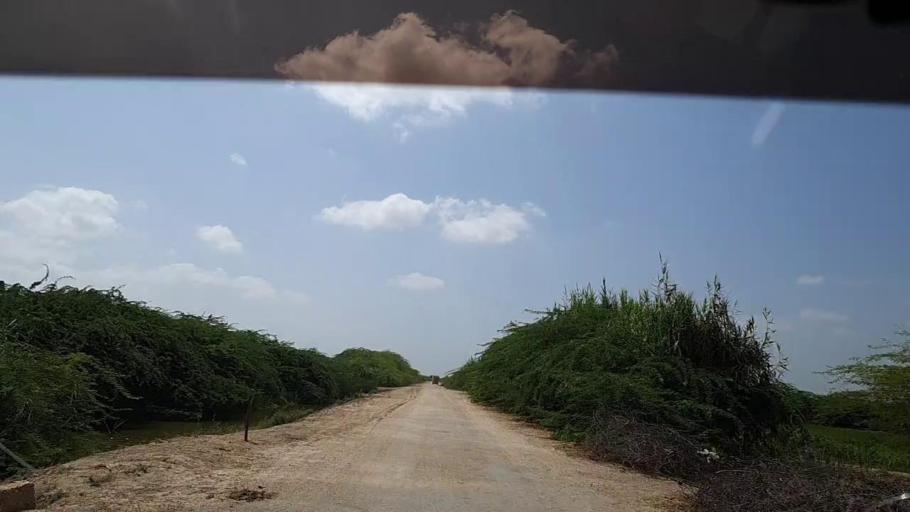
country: PK
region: Sindh
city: Badin
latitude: 24.5645
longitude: 68.7528
